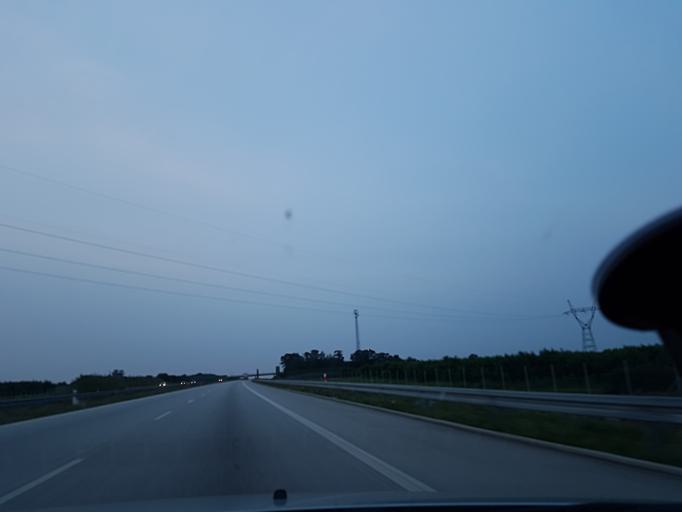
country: PL
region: Lodz Voivodeship
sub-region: Powiat zgierski
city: Strykow
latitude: 51.8621
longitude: 19.6575
